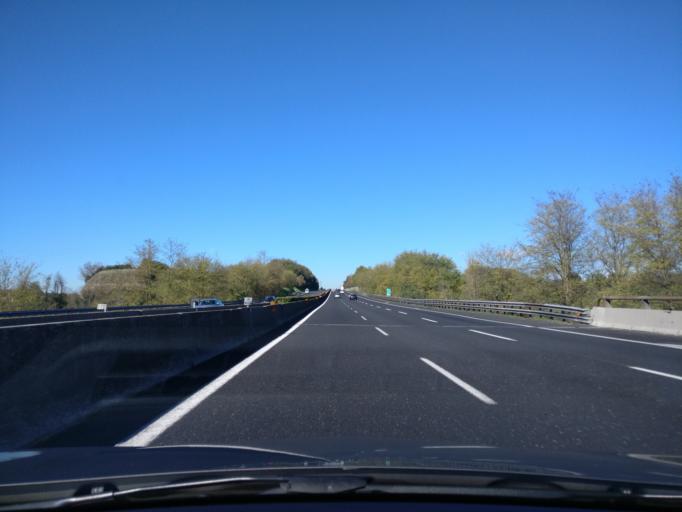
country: IT
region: Latium
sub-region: Provincia di Frosinone
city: Paliano
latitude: 41.7381
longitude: 13.0827
